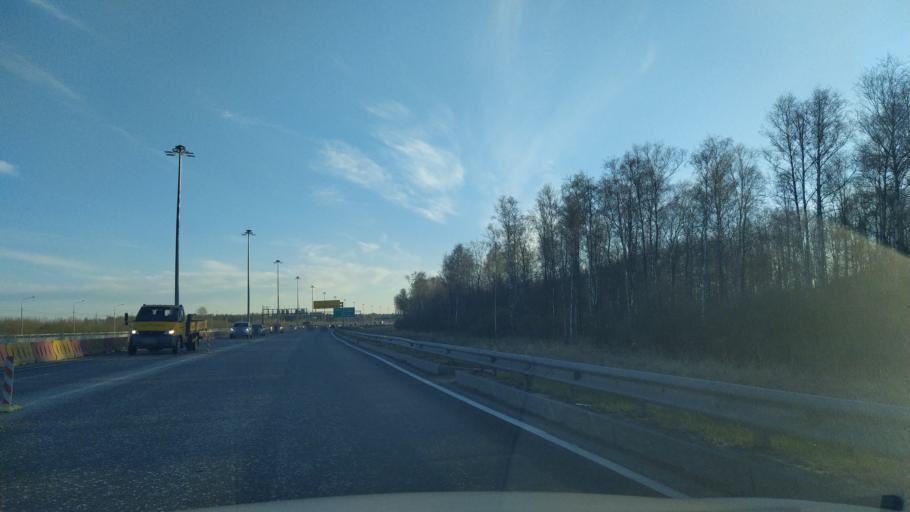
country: RU
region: St.-Petersburg
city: Levashovo
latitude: 60.0690
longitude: 30.1723
